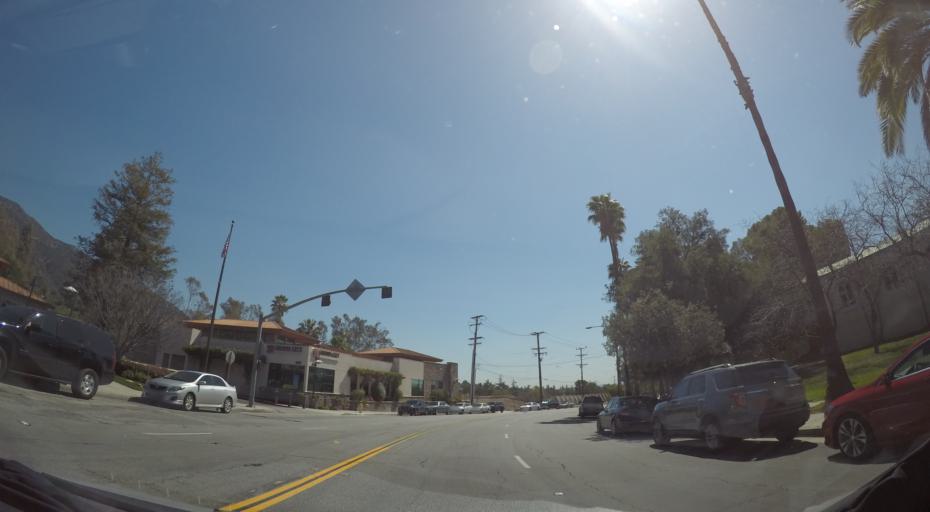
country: US
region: California
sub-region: Los Angeles County
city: East Pasadena
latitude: 34.1691
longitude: -118.0955
